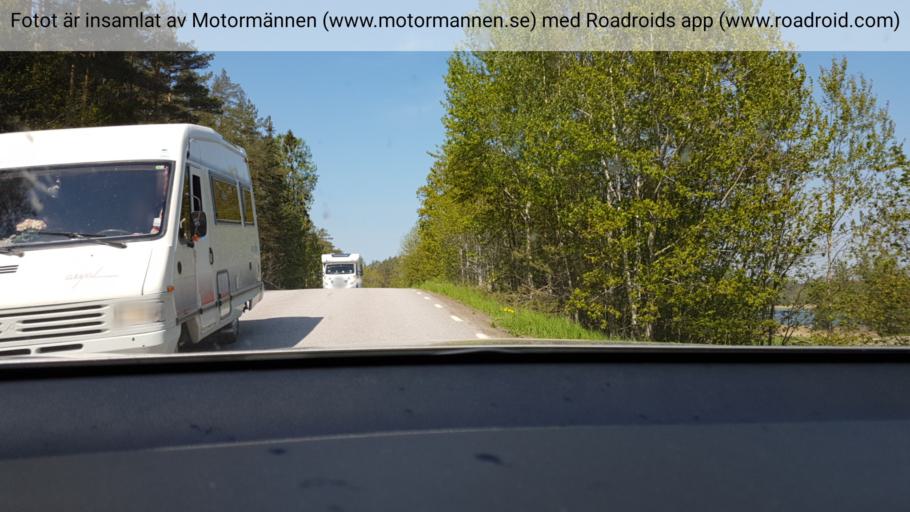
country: SE
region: Kalmar
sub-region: Vasterviks Kommun
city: Vaestervik
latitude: 57.8298
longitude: 16.5514
